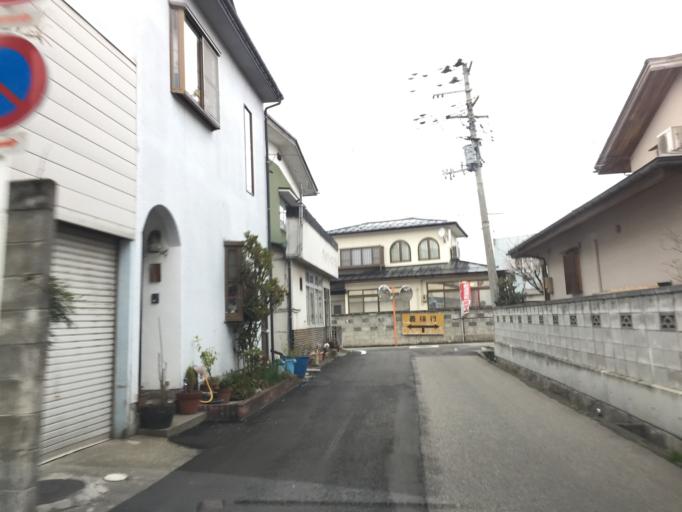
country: JP
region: Fukushima
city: Kitakata
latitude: 37.5002
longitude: 139.9168
